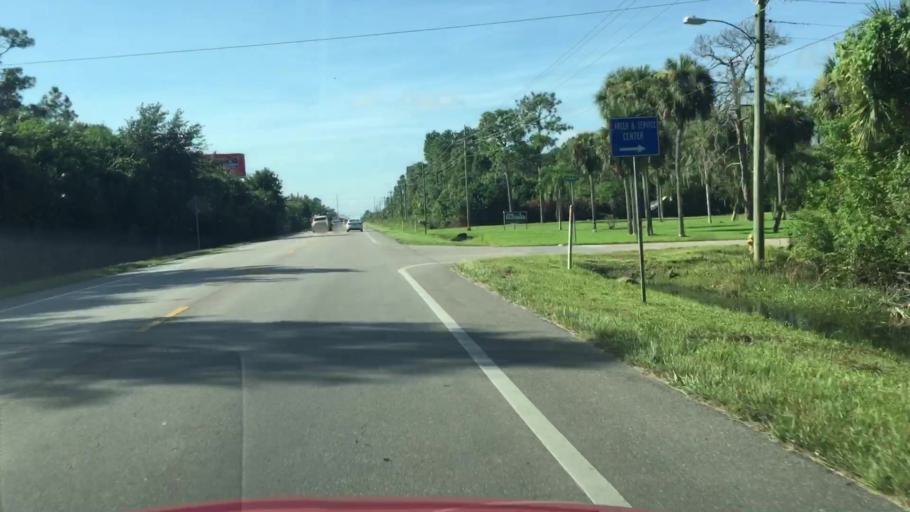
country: US
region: Florida
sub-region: Collier County
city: Immokalee
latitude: 26.4043
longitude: -81.4172
